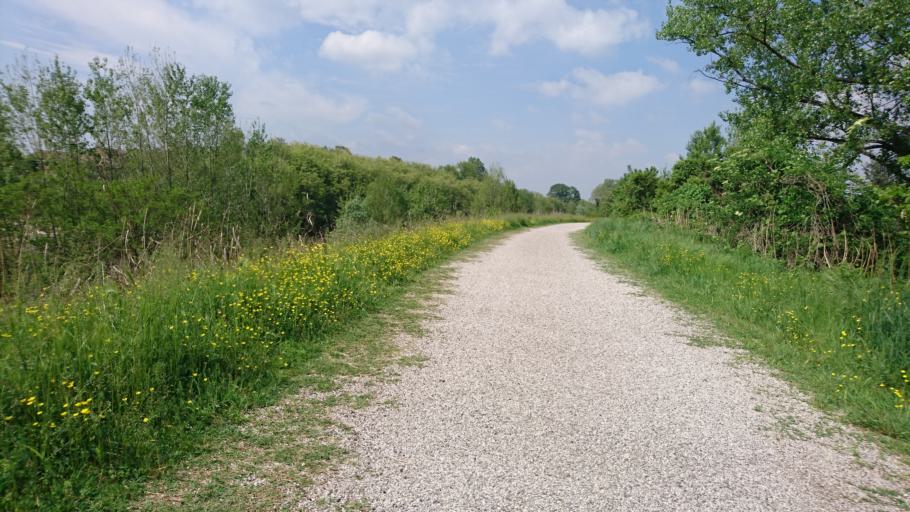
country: IT
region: Veneto
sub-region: Provincia di Padova
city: Vigodarzere
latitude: 45.4489
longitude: 11.8867
